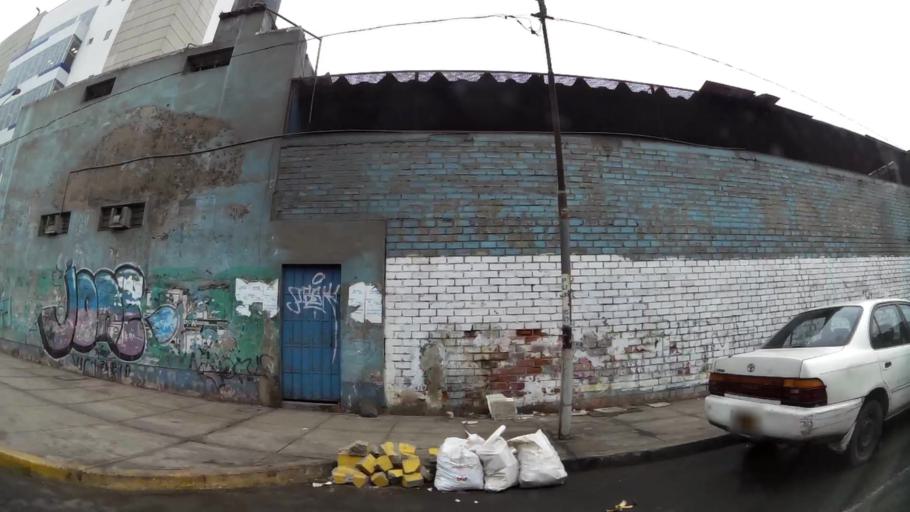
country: PE
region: Lima
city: Lima
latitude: -12.0618
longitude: -77.0230
